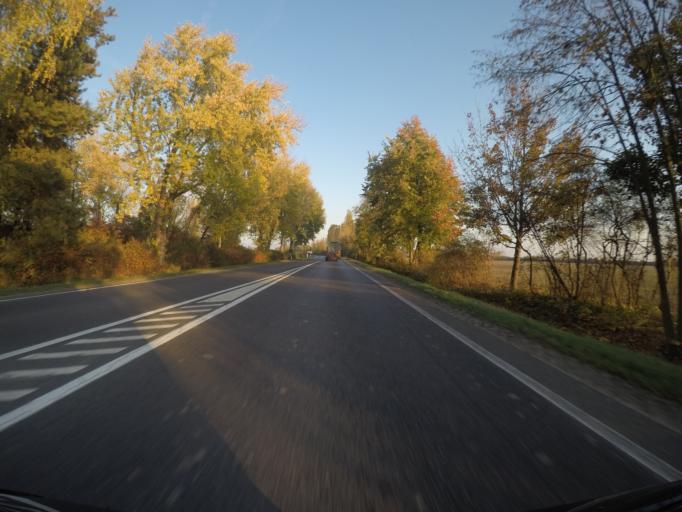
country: HU
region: Baranya
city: Szentlorinc
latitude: 46.0397
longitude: 17.9296
